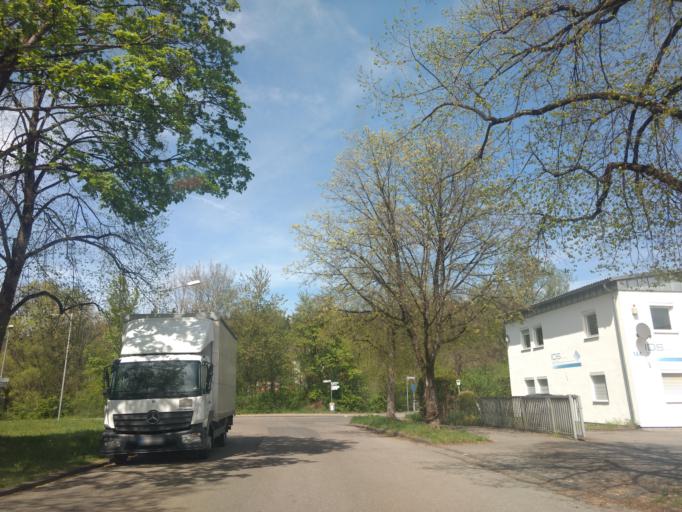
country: DE
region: Baden-Wuerttemberg
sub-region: Regierungsbezirk Stuttgart
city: Schwabisch Gmund
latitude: 48.7876
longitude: 9.7661
